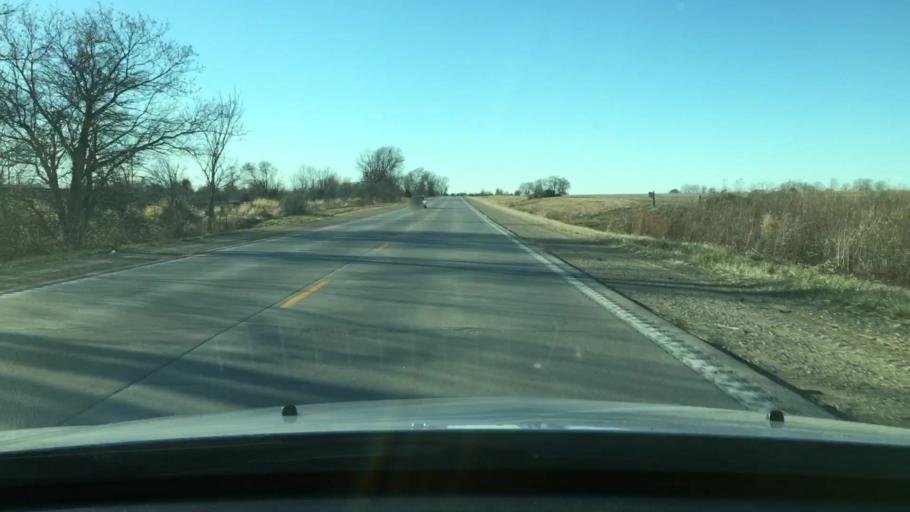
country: US
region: Missouri
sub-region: Audrain County
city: Mexico
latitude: 39.1906
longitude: -92.0006
